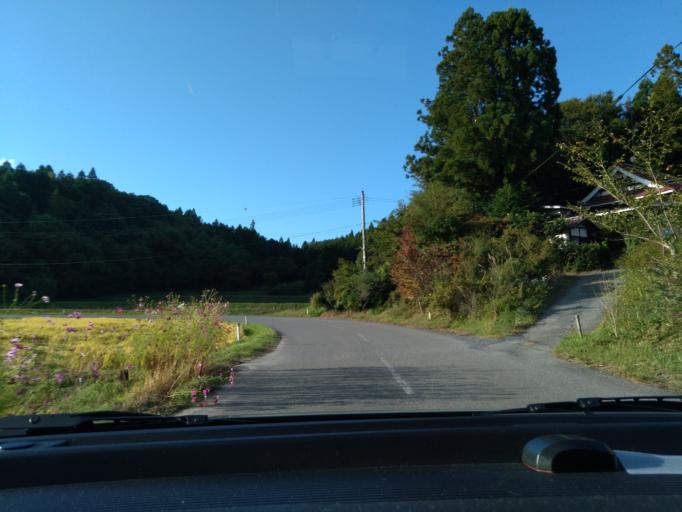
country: JP
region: Iwate
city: Ichinoseki
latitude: 38.8702
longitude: 141.1749
